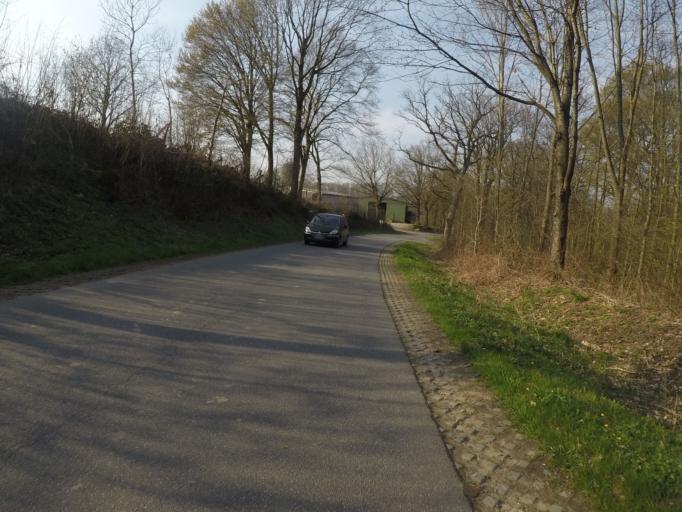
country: DE
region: Schleswig-Holstein
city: Kukels
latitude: 53.8870
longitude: 10.2406
